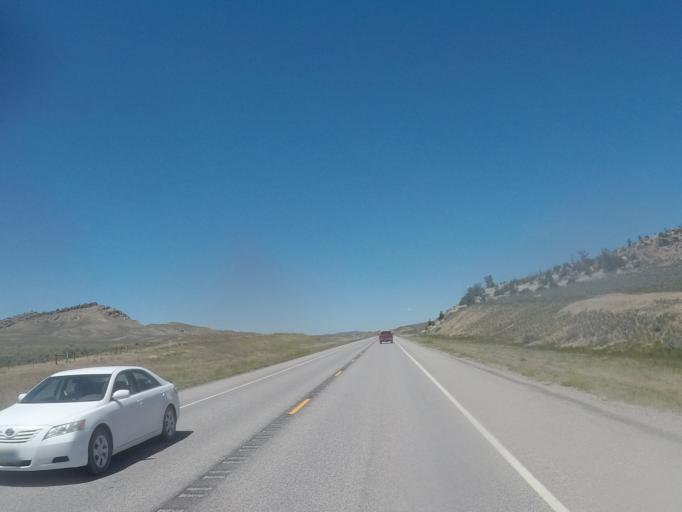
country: US
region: Montana
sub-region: Carbon County
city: Red Lodge
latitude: 45.2089
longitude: -108.8696
